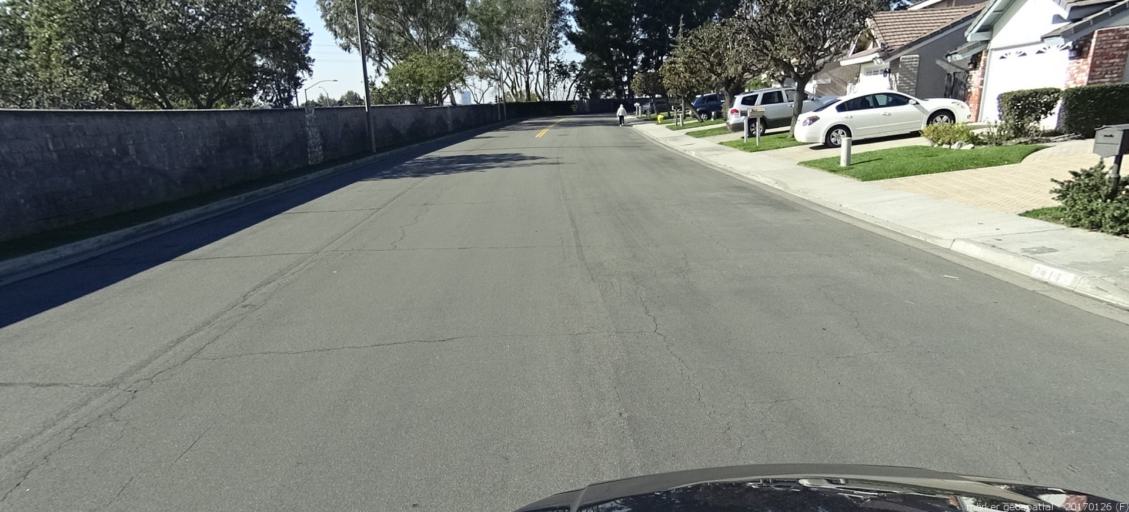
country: US
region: California
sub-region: Orange County
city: Lake Forest
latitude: 33.6447
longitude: -117.7095
